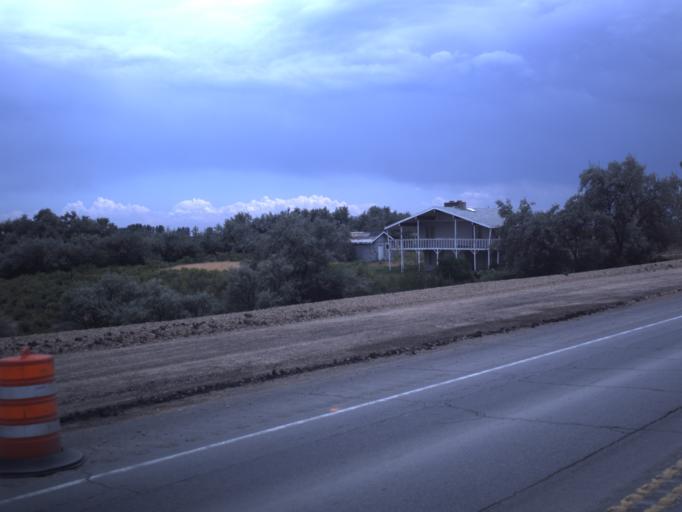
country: US
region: Utah
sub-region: Duchesne County
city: Roosevelt
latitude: 40.2415
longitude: -110.0675
